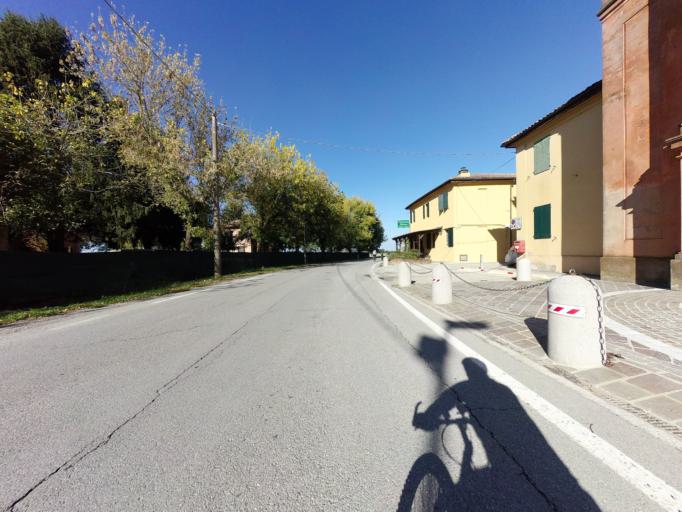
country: IT
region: Emilia-Romagna
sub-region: Provincia di Bologna
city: Progresso
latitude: 44.5715
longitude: 11.3916
